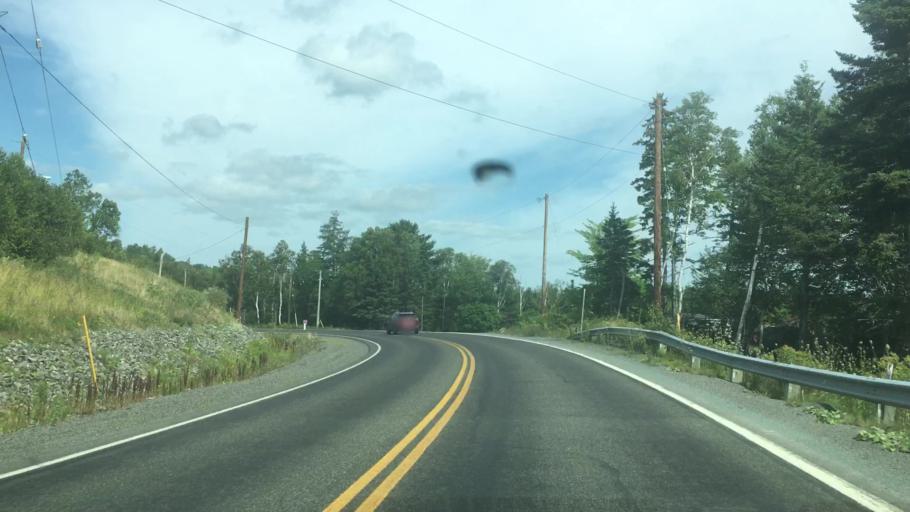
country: CA
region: Nova Scotia
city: Sydney Mines
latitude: 46.2122
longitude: -60.6200
